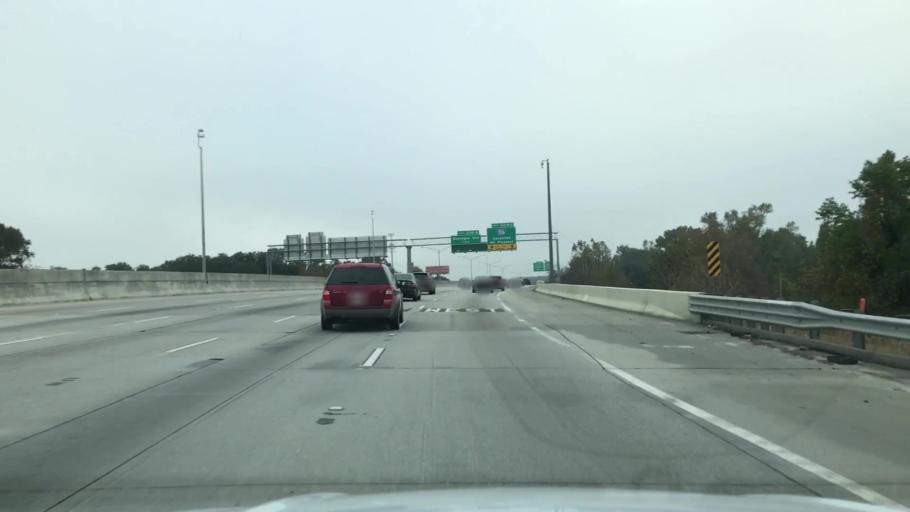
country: US
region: South Carolina
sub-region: Berkeley County
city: Hanahan
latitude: 32.8931
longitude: -80.0188
